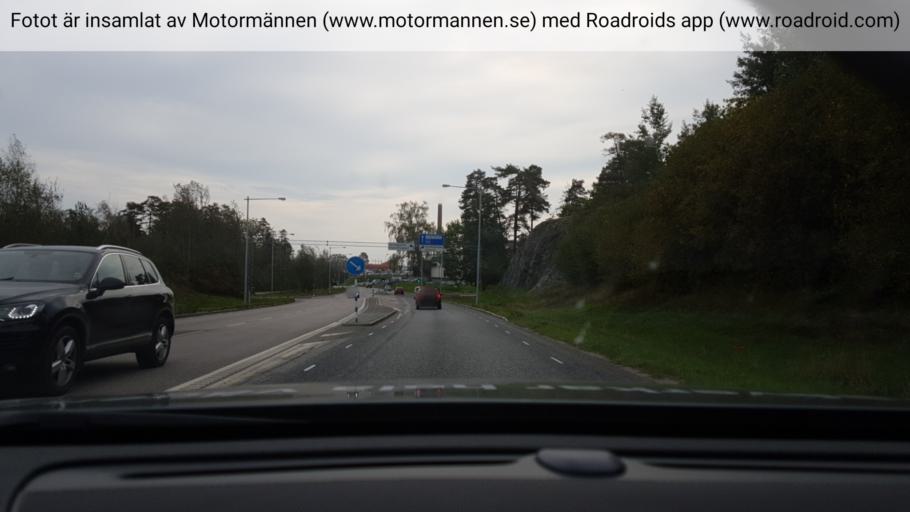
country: SE
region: Stockholm
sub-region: Nynashamns Kommun
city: Nynashamn
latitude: 58.9160
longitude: 17.9564
